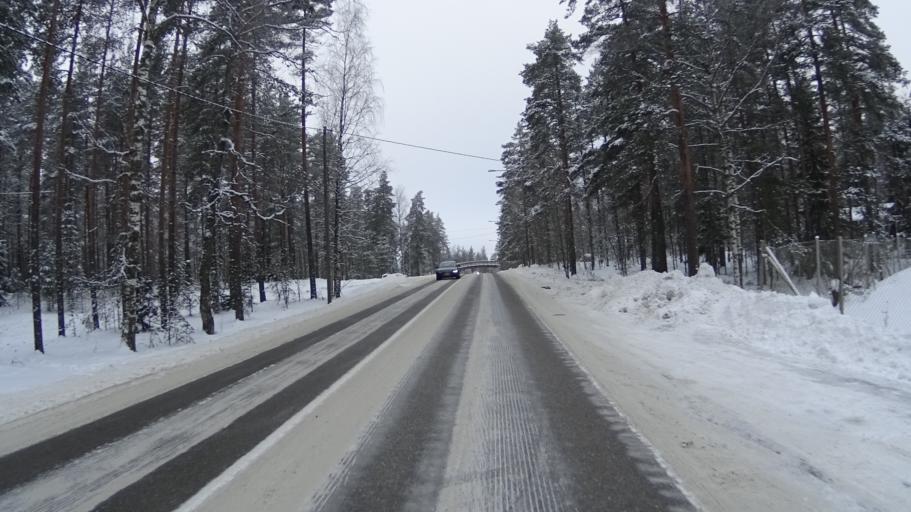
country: FI
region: Uusimaa
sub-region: Helsinki
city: Vihti
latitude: 60.3391
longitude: 24.3094
